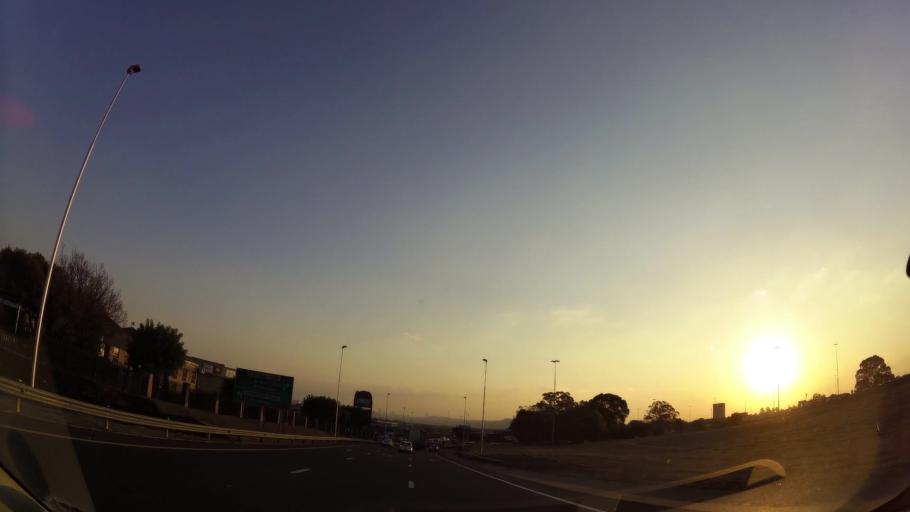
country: ZA
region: Gauteng
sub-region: Ekurhuleni Metropolitan Municipality
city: Germiston
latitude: -26.1640
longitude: 28.1690
